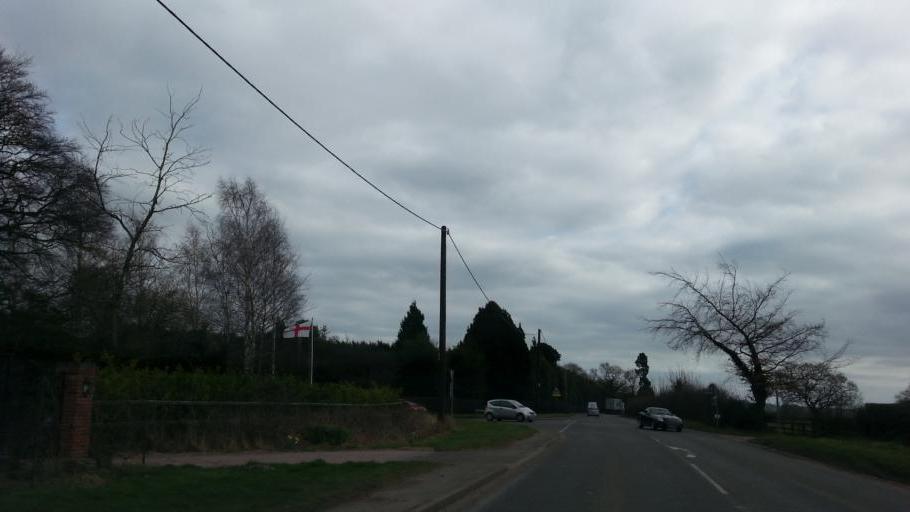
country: GB
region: England
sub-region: Staffordshire
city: Colwich
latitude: 52.8288
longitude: -2.0221
